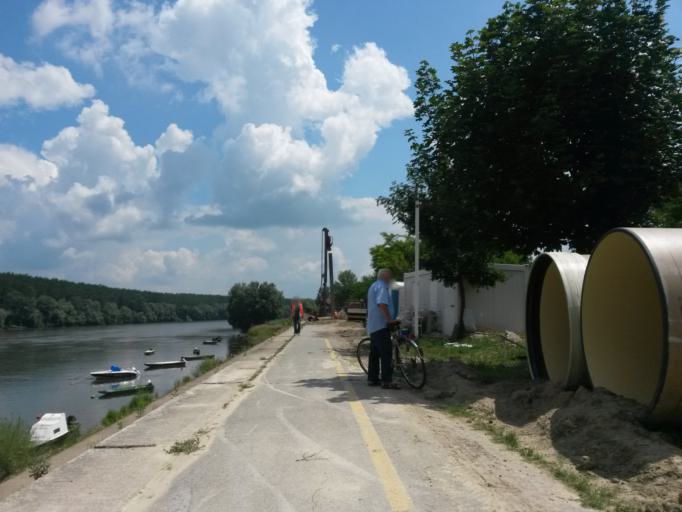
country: HR
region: Osjecko-Baranjska
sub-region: Grad Osijek
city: Osijek
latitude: 45.5617
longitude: 18.7262
